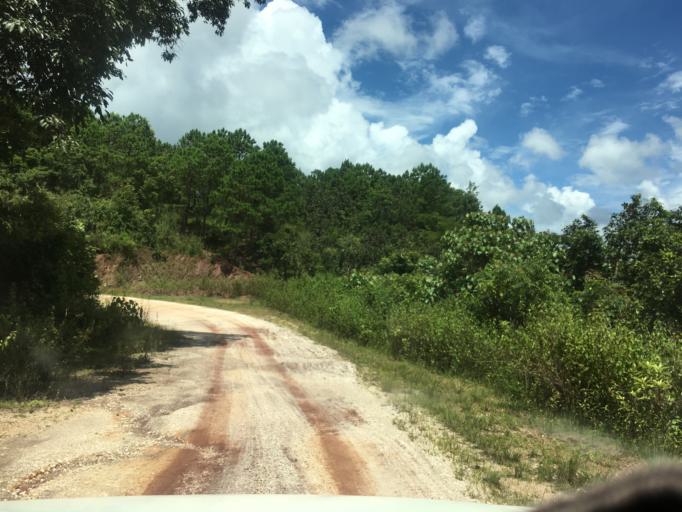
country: LA
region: Xiangkhoang
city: Phonsavan
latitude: 19.6848
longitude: 103.0956
